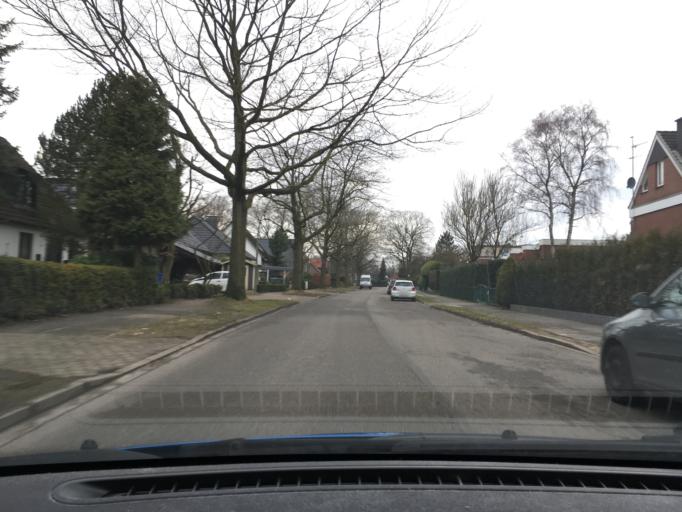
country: DE
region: Schleswig-Holstein
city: Wedel
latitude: 53.5910
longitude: 9.7219
